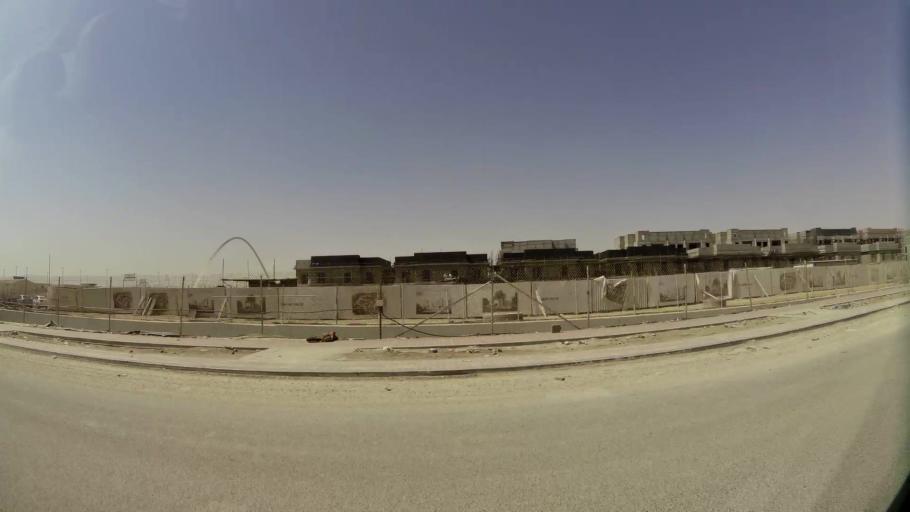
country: QA
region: Baladiyat Umm Salal
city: Umm Salal Muhammad
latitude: 25.4045
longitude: 51.5177
